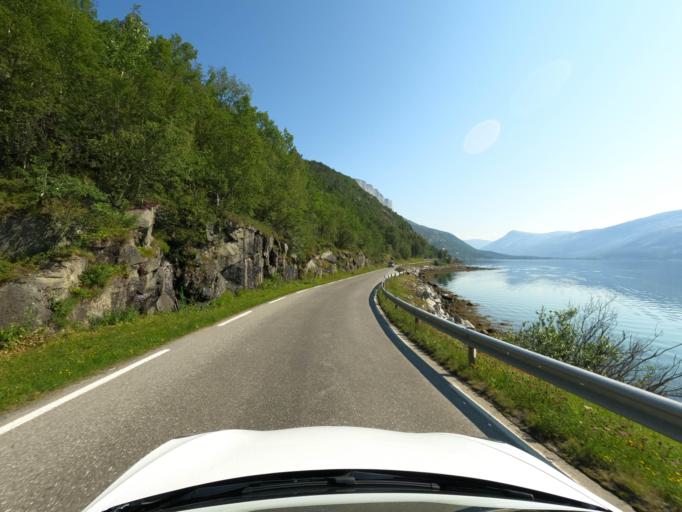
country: NO
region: Nordland
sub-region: Narvik
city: Narvik
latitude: 68.2905
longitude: 17.3612
